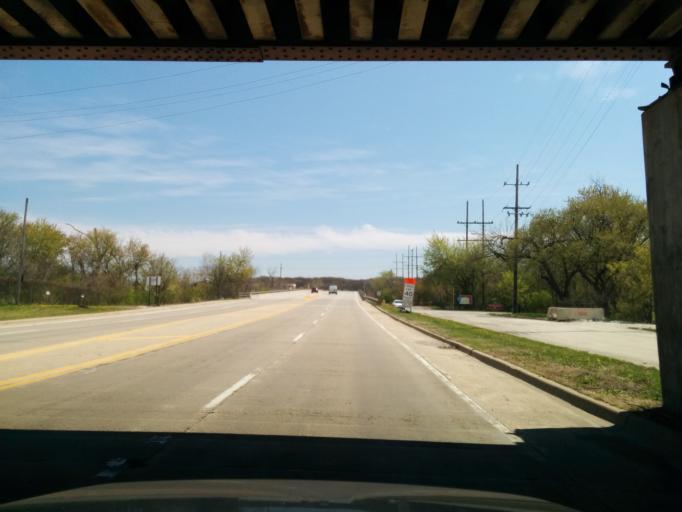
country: US
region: Illinois
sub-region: Cook County
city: Willow Springs
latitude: 41.7365
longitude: -87.8829
